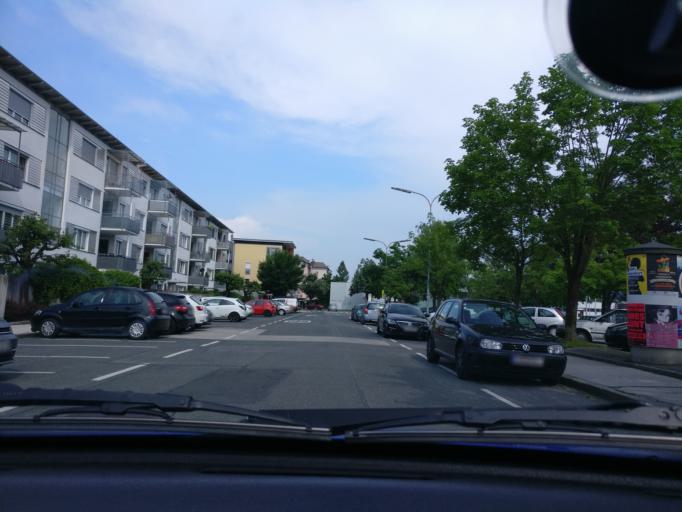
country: AT
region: Carinthia
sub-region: Klagenfurt am Woerthersee
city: Klagenfurt am Woerthersee
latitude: 46.6089
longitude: 14.2897
